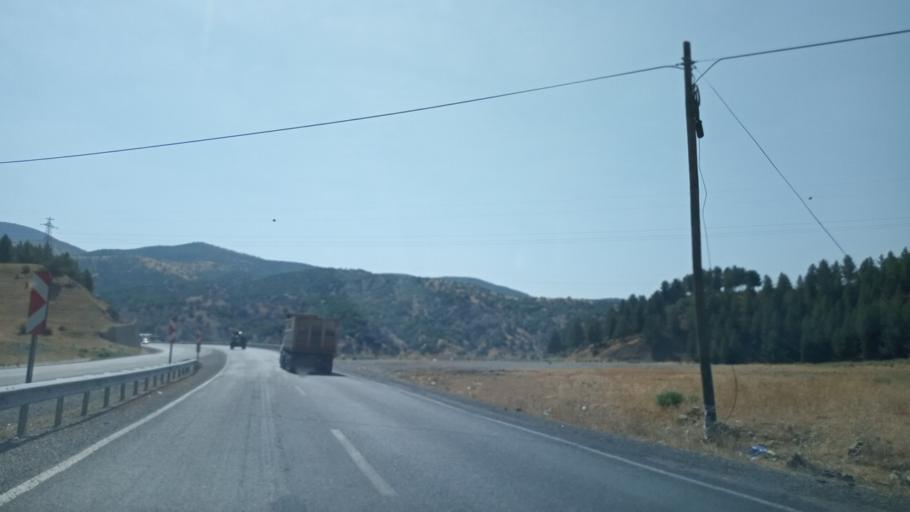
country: TR
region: Siirt
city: Baykan
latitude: 38.1332
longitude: 41.7452
